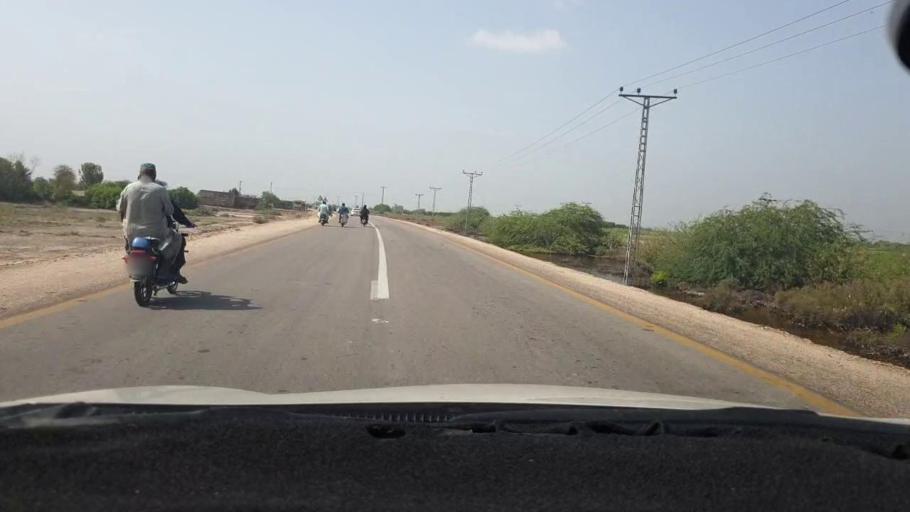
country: PK
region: Sindh
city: Mirpur Khas
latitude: 25.6925
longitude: 69.1171
